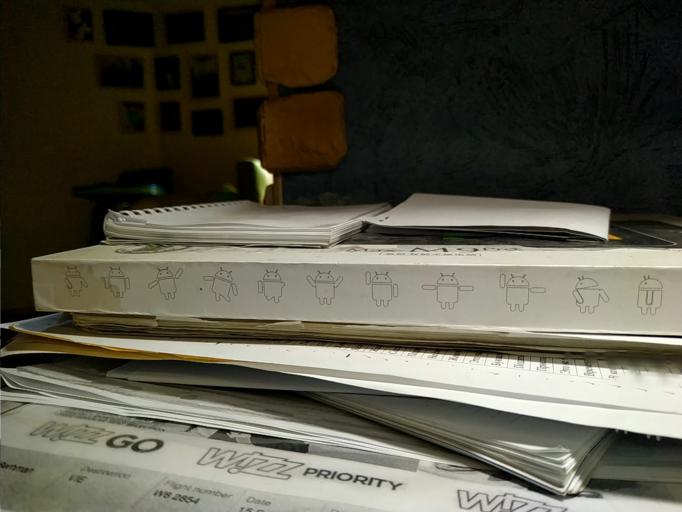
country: RU
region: Novgorod
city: Poddor'ye
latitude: 57.5230
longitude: 30.9140
